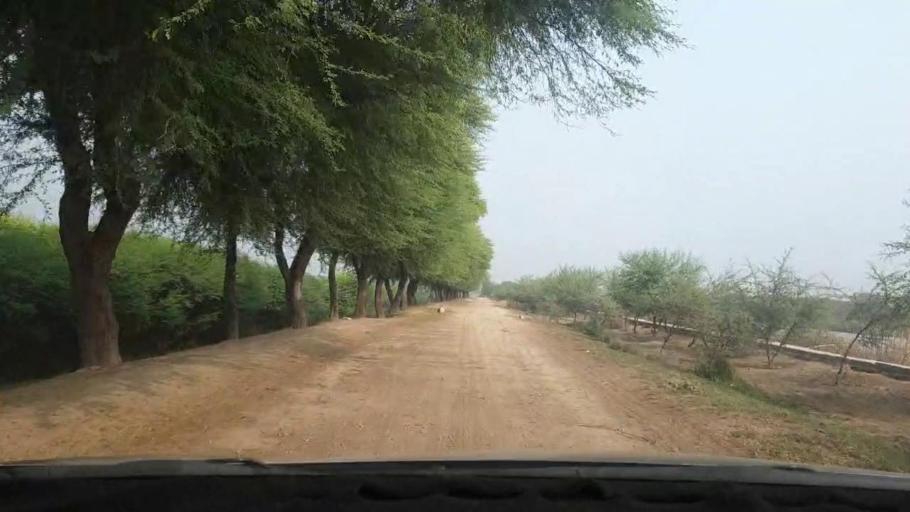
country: PK
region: Sindh
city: Matiari
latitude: 25.6464
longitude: 68.5605
